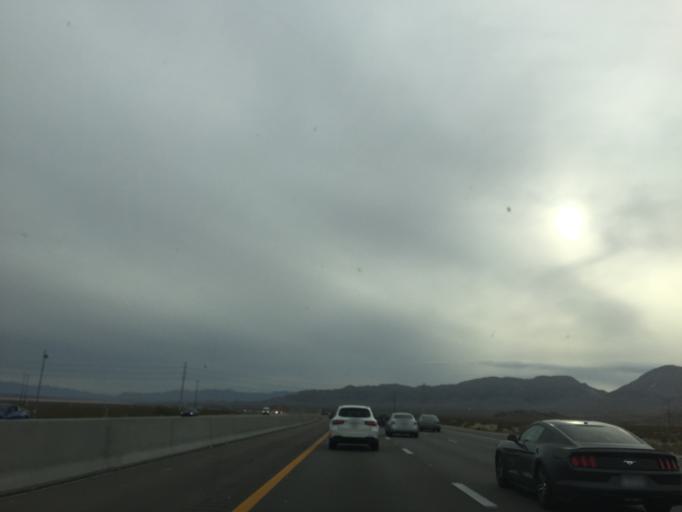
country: US
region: Nevada
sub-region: Clark County
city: Sandy Valley
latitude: 35.7486
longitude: -115.3521
